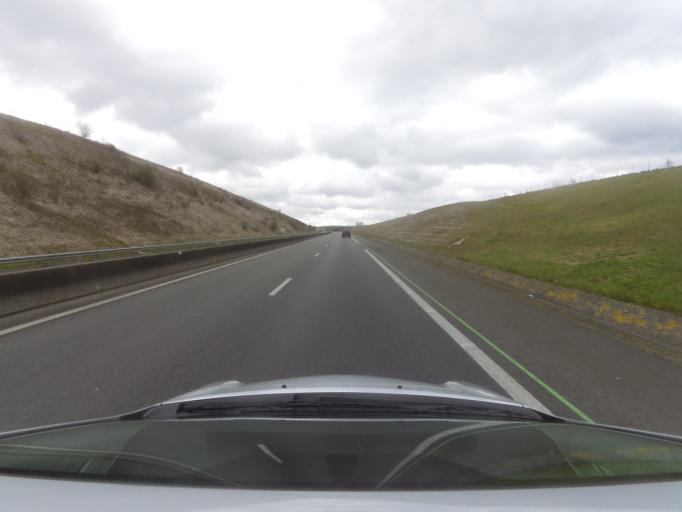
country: FR
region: Nord-Pas-de-Calais
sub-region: Departement du Pas-de-Calais
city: Nesles
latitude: 50.6247
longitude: 1.6609
